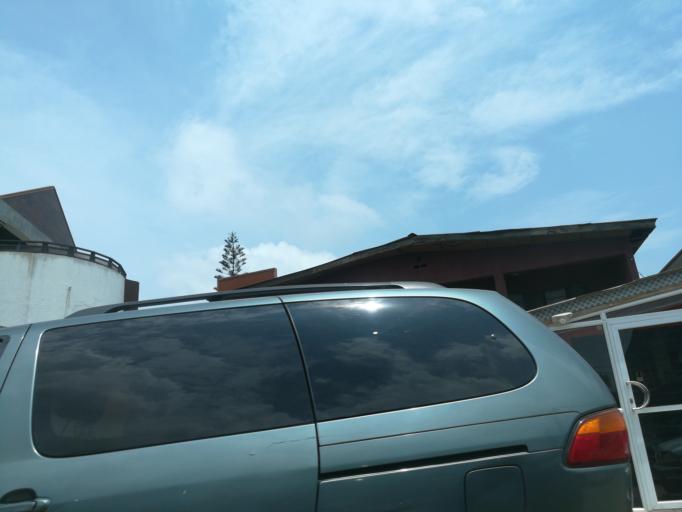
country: NG
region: Lagos
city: Oshodi
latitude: 6.5493
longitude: 3.3293
